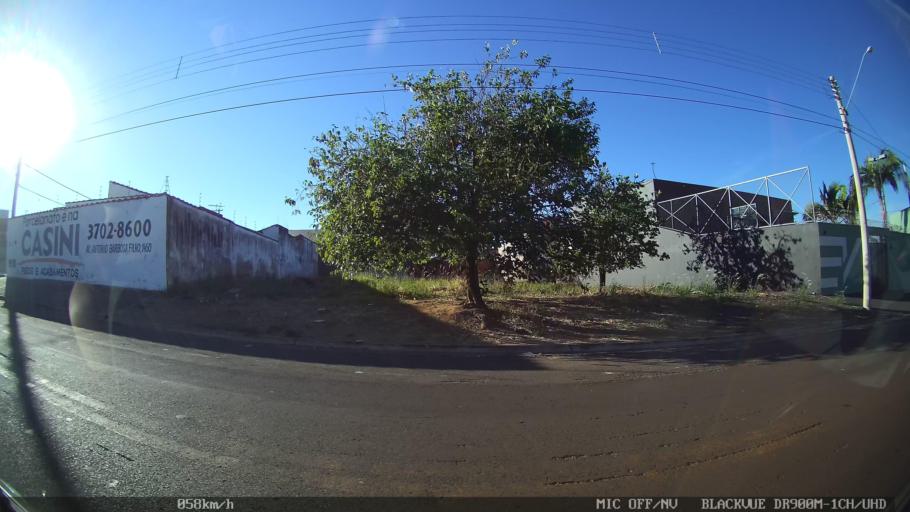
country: BR
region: Sao Paulo
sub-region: Franca
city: Franca
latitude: -20.5728
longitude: -47.4075
